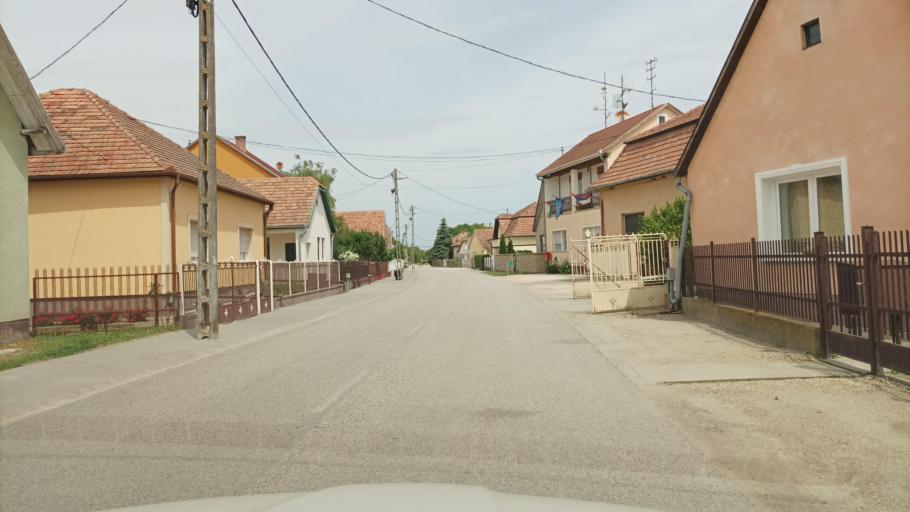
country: HU
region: Fejer
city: Adony
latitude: 47.1157
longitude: 18.8962
